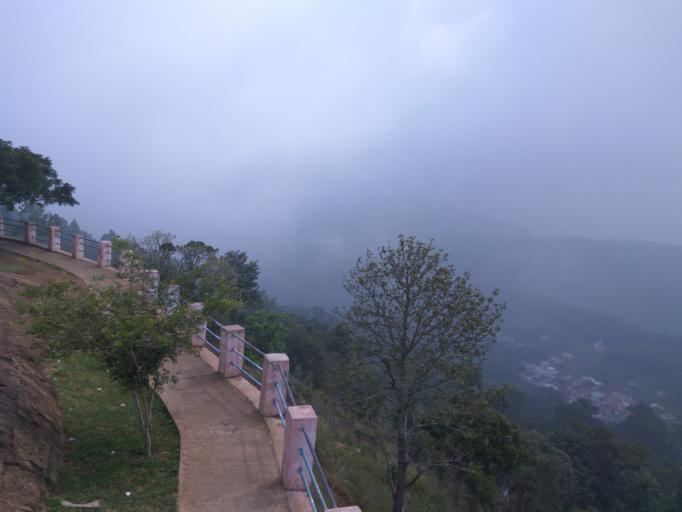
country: IN
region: Tamil Nadu
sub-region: Salem
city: Salem
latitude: 11.7663
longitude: 78.2390
